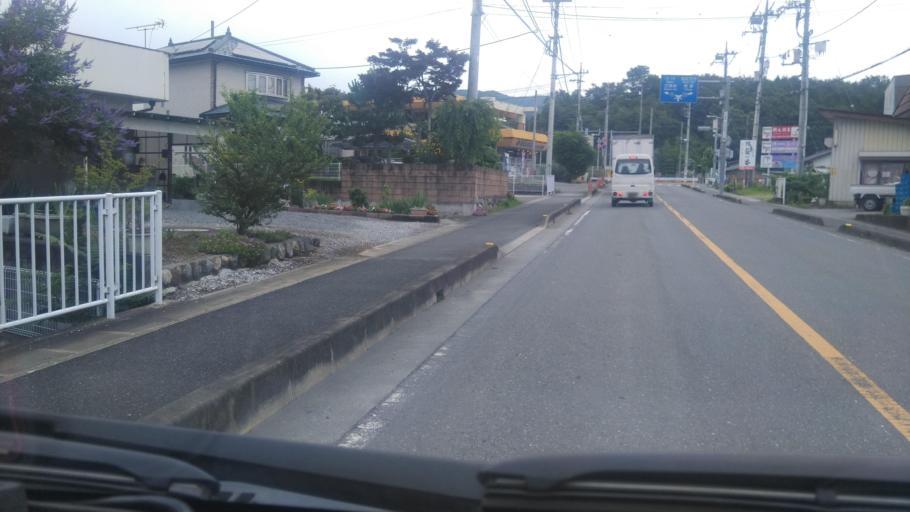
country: JP
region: Saitama
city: Chichibu
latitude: 36.0207
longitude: 139.1119
